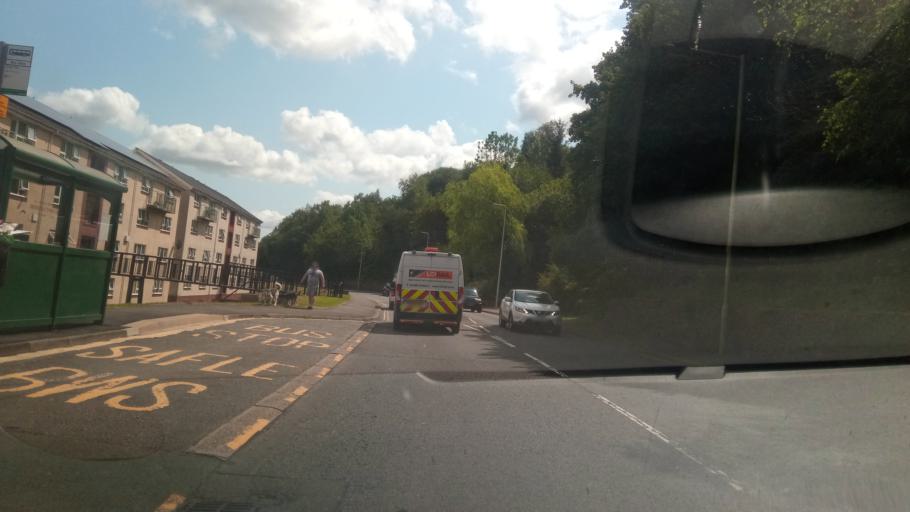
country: GB
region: Wales
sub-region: Rhondda Cynon Taf
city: Tonypandy
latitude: 51.6160
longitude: -3.4352
